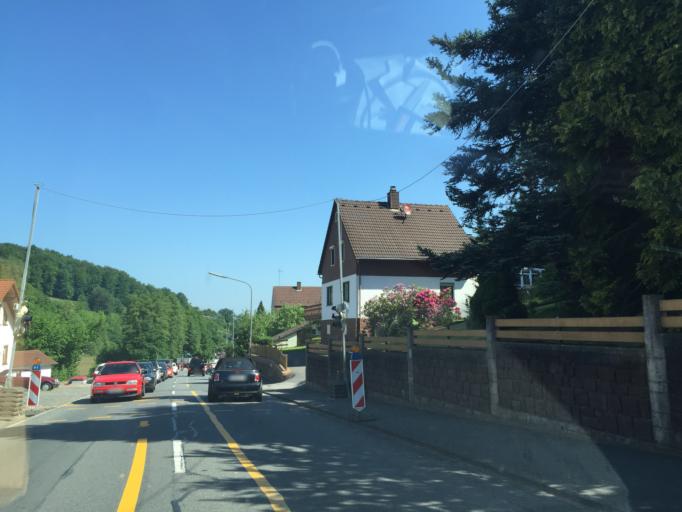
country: DE
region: Hesse
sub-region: Regierungsbezirk Darmstadt
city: Erbach
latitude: 49.6254
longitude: 8.9941
